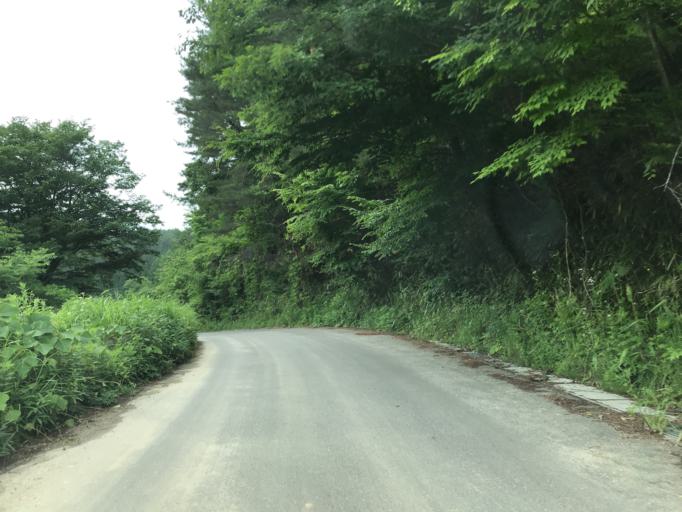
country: JP
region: Fukushima
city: Funehikimachi-funehiki
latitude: 37.4383
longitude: 140.7811
